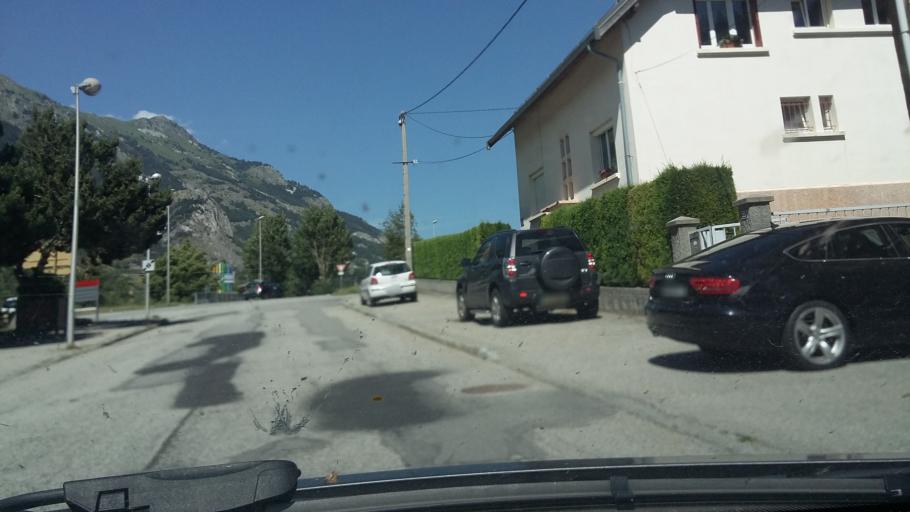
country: FR
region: Rhone-Alpes
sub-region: Departement de la Savoie
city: Modane
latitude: 45.2043
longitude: 6.6773
